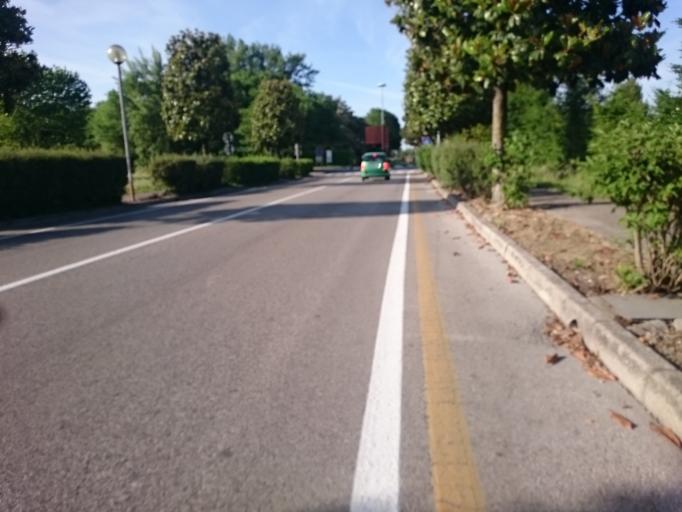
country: IT
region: Veneto
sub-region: Provincia di Padova
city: Abano Terme
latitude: 45.3568
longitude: 11.7935
